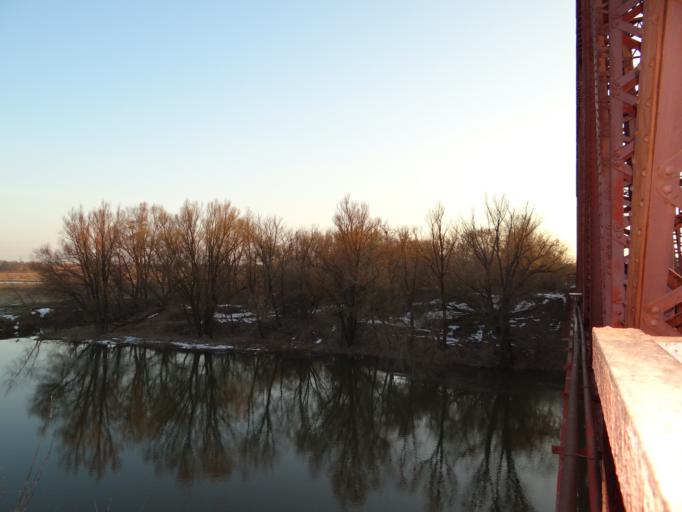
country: RU
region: Kursk
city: Kursk
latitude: 51.6866
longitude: 36.1133
